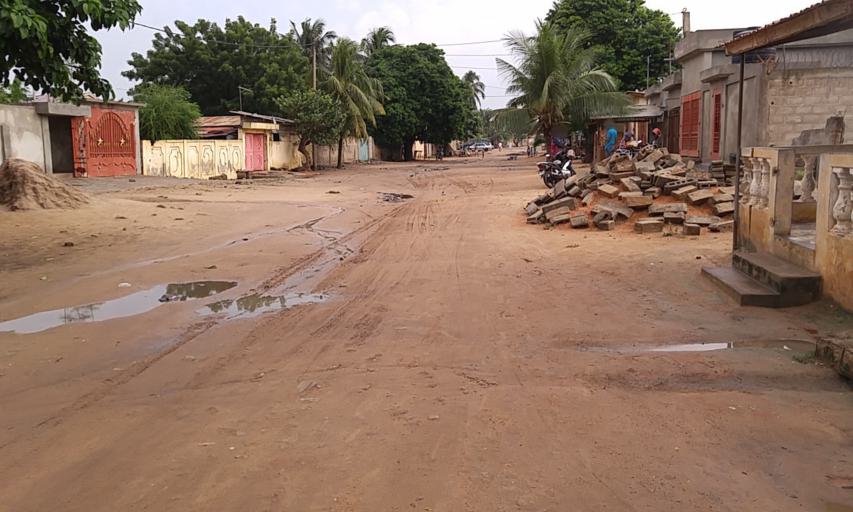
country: TG
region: Maritime
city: Lome
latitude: 6.1755
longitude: 1.1717
